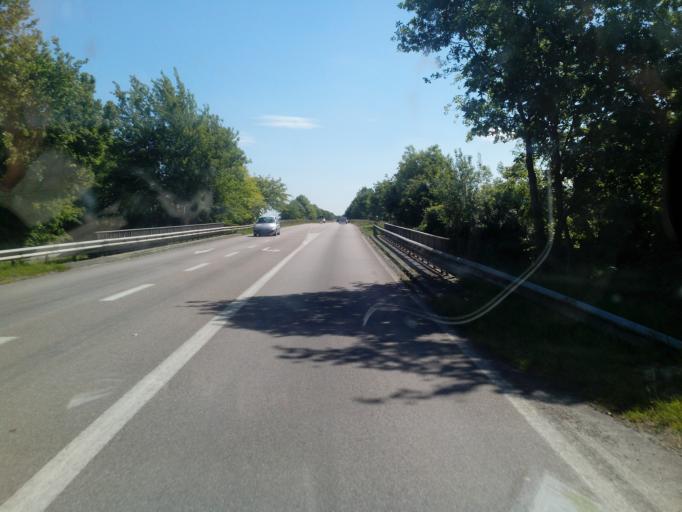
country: FR
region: Haute-Normandie
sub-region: Departement de l'Eure
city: Beuzeville
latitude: 49.3785
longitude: 0.3996
